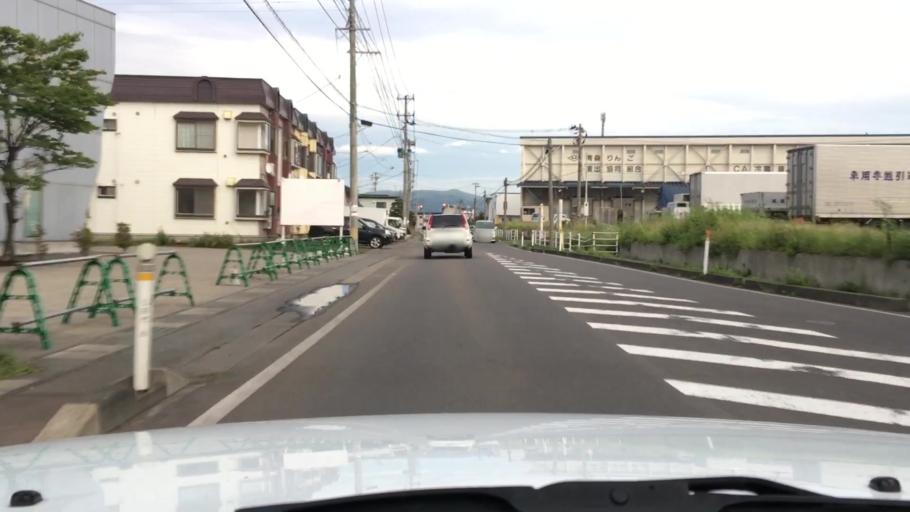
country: JP
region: Aomori
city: Hirosaki
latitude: 40.5952
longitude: 140.5051
